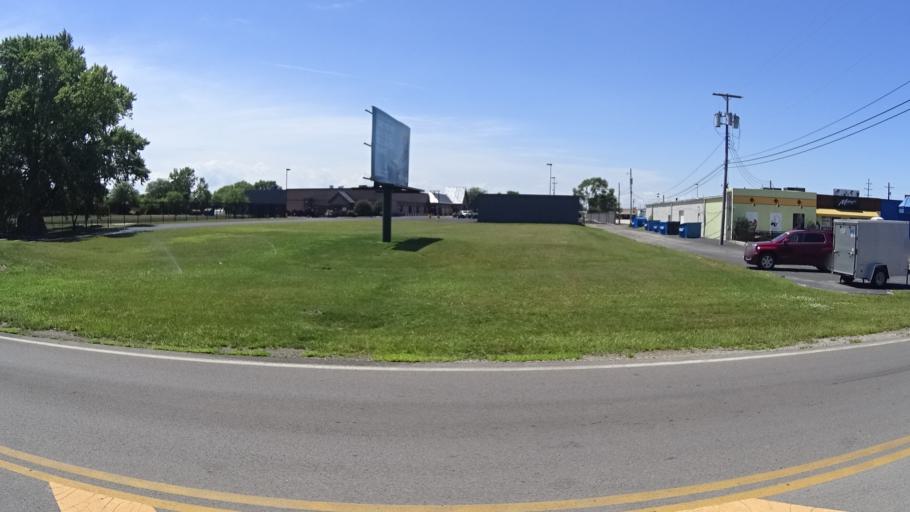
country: US
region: Ohio
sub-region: Erie County
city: Sandusky
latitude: 41.4321
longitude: -82.7052
